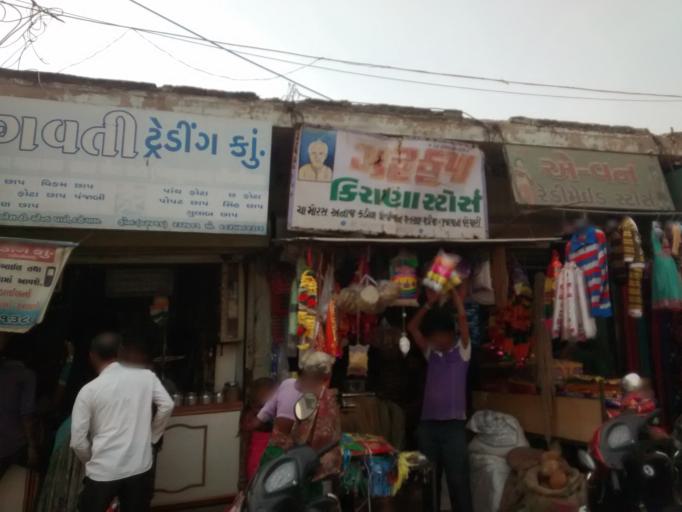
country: IN
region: Gujarat
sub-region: Gandhinagar
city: Dahegam
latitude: 23.1699
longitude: 72.8206
